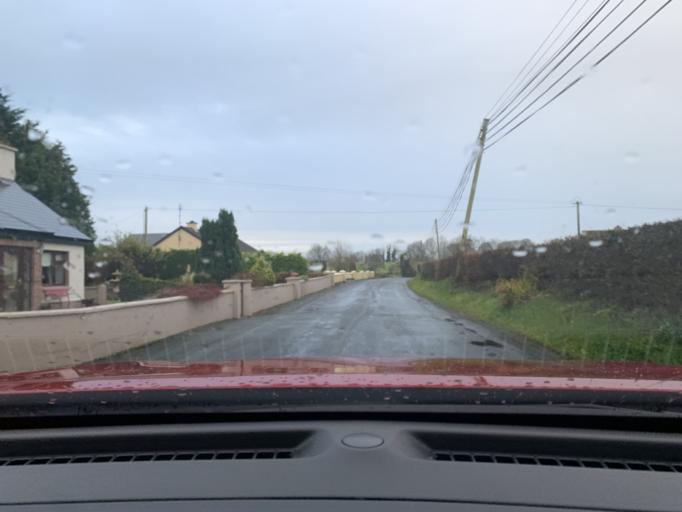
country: IE
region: Connaught
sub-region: Sligo
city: Ballymote
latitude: 54.0027
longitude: -8.4975
